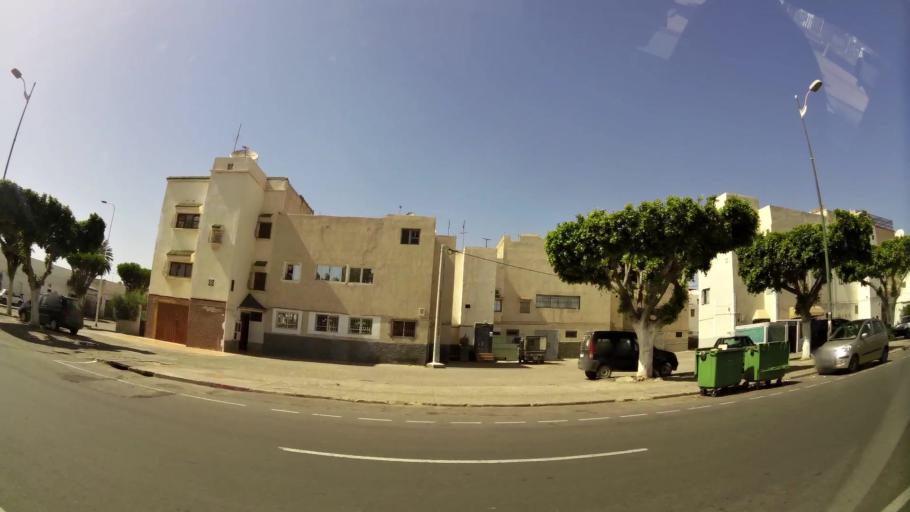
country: MA
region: Oued ed Dahab-Lagouira
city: Dakhla
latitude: 30.4137
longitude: -9.5719
